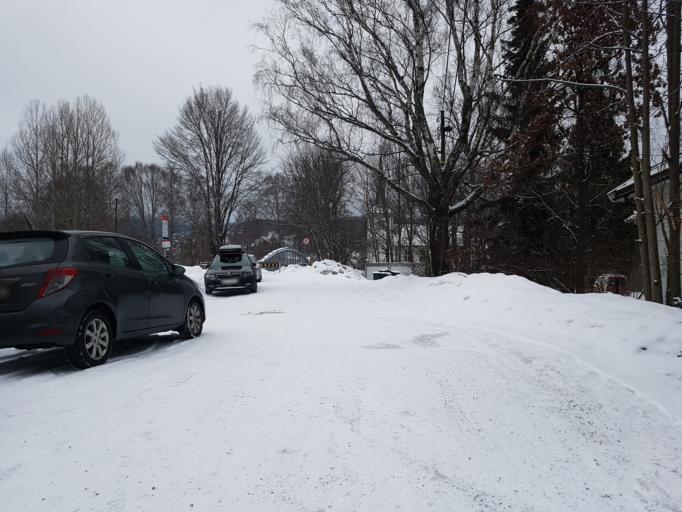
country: NO
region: Buskerud
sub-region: Drammen
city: Drammen
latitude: 59.7414
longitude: 10.1866
